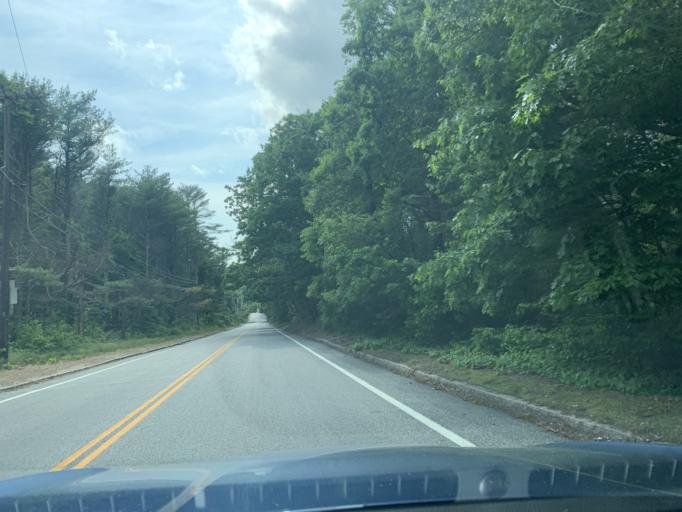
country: US
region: Rhode Island
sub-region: Kent County
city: Coventry
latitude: 41.7076
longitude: -71.7576
